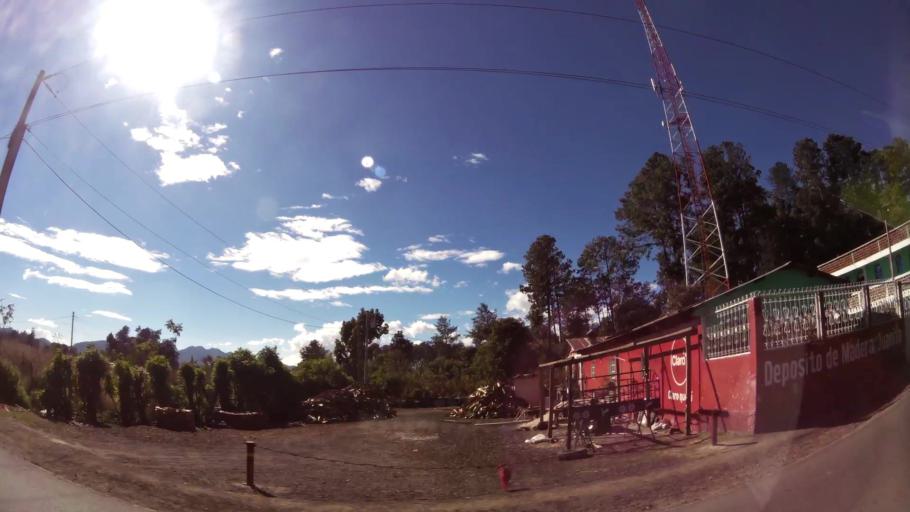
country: GT
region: Solola
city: Solola
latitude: 14.8067
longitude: -91.1797
